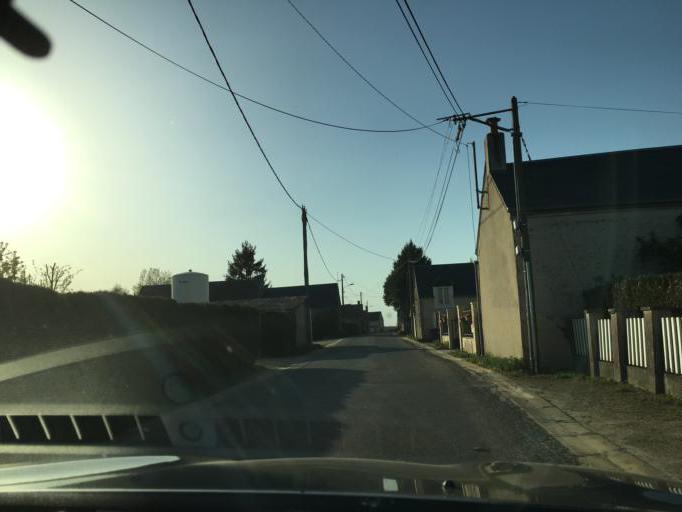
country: FR
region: Centre
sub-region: Departement du Loir-et-Cher
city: Ouzouer-le-Marche
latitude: 47.8990
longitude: 1.5744
